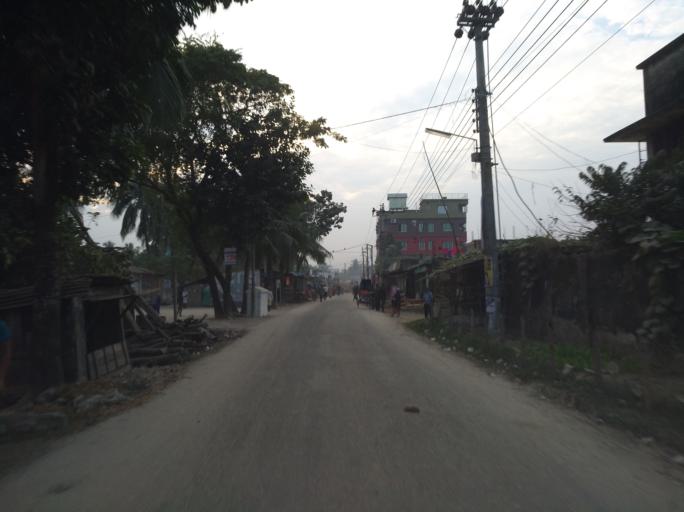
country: BD
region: Khulna
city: Khulna
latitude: 22.8501
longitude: 89.5469
